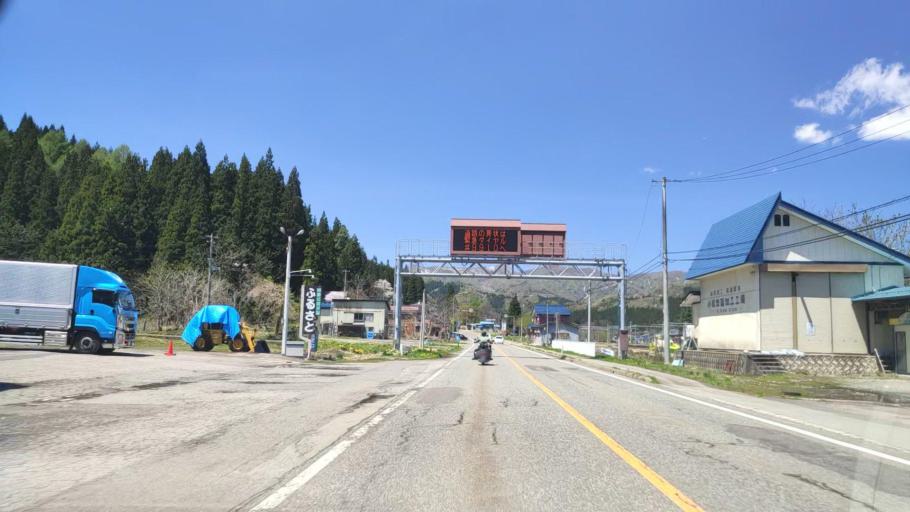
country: JP
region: Akita
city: Yuzawa
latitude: 39.0483
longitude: 140.4156
